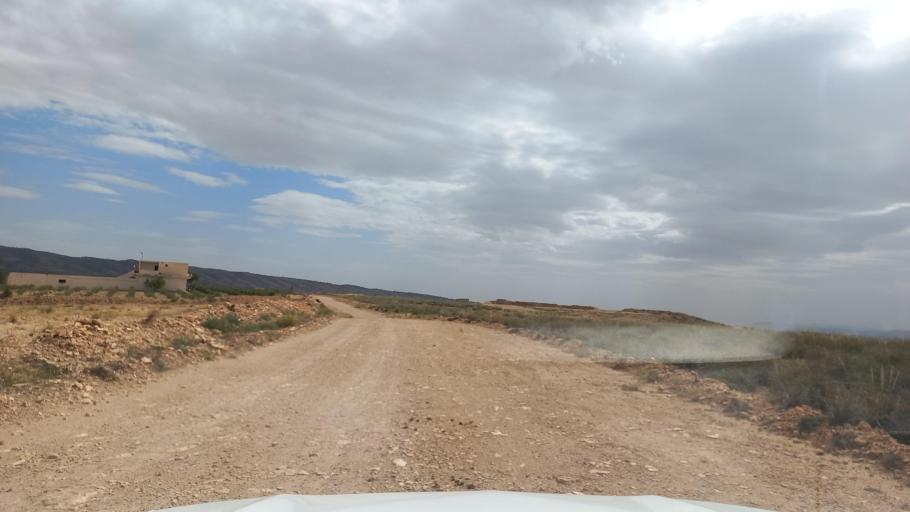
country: TN
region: Al Qasrayn
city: Sbiba
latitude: 35.3608
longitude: 9.1126
